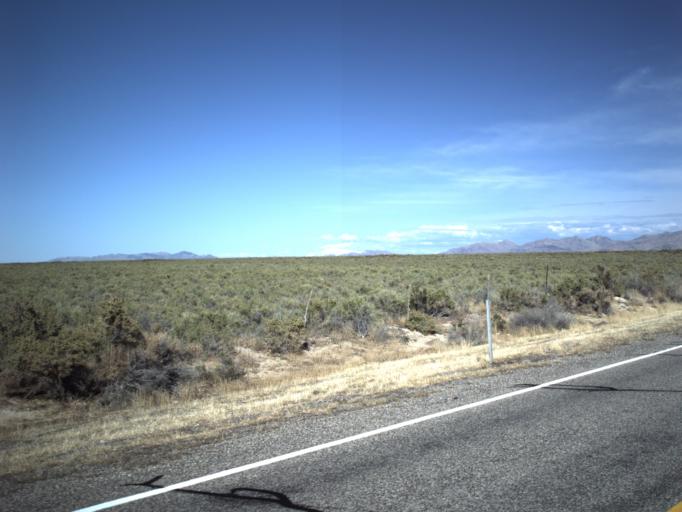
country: US
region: Utah
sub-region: Millard County
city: Delta
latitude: 39.3531
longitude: -112.5121
